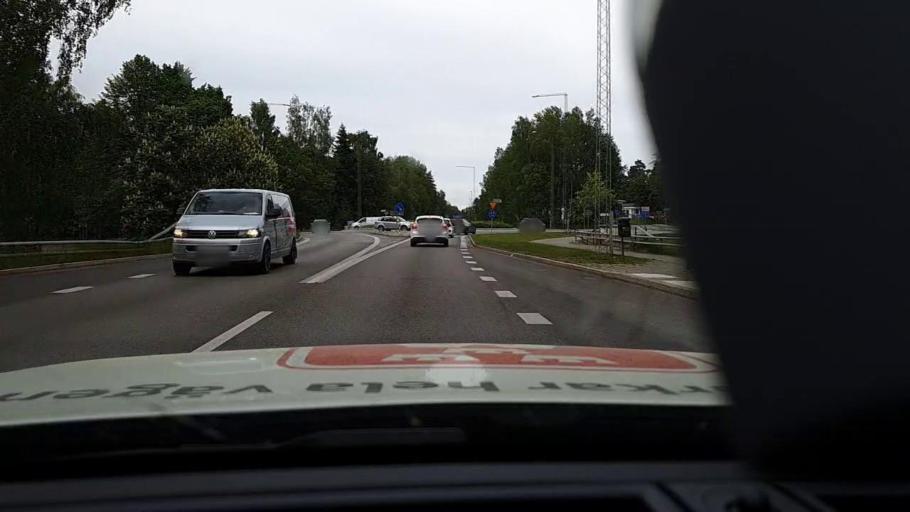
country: SE
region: Stockholm
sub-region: Haninge Kommun
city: Haninge
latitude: 59.1993
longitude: 18.1888
